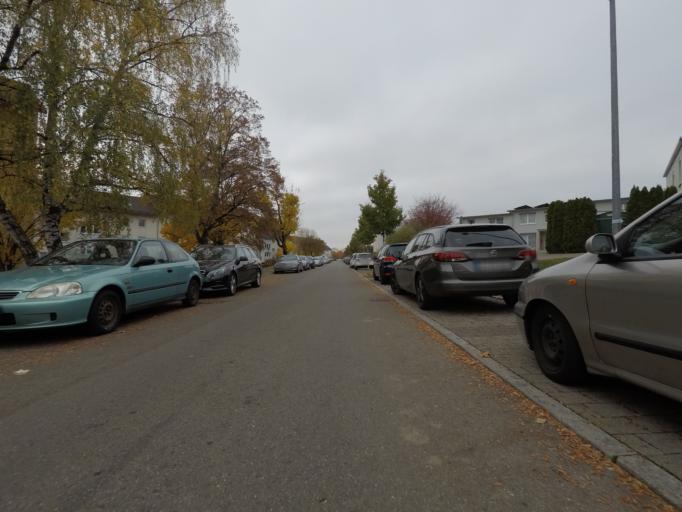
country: DE
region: Baden-Wuerttemberg
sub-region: Tuebingen Region
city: Reutlingen
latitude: 48.5127
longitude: 9.2068
